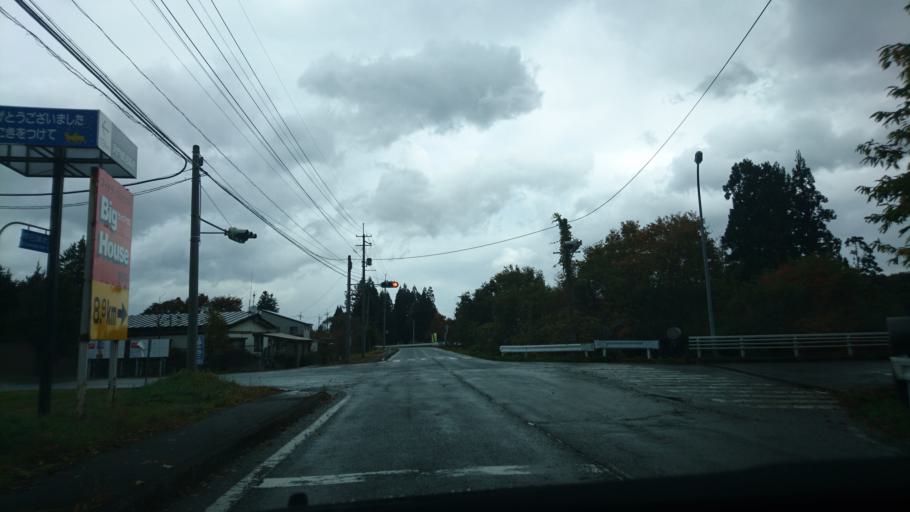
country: JP
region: Iwate
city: Shizukuishi
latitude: 39.6447
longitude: 140.9495
